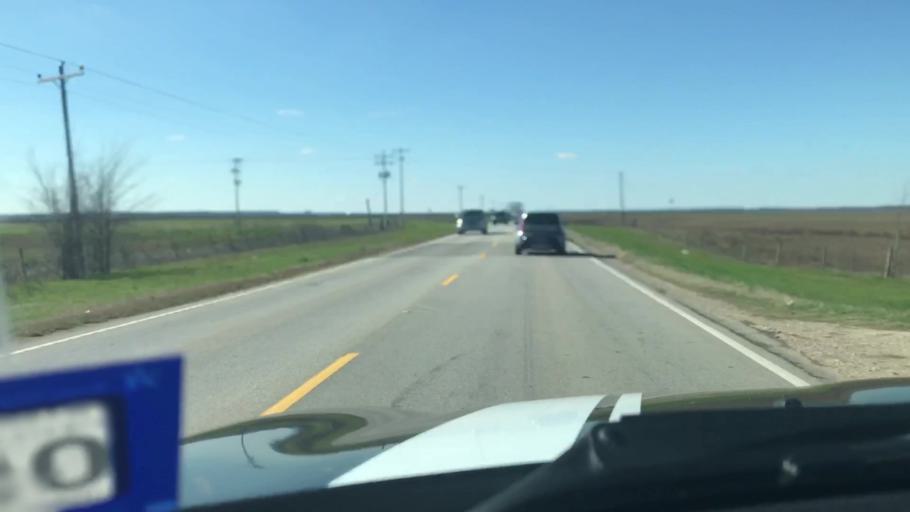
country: US
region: Texas
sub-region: Robertson County
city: Hearne
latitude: 30.8783
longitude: -96.6443
